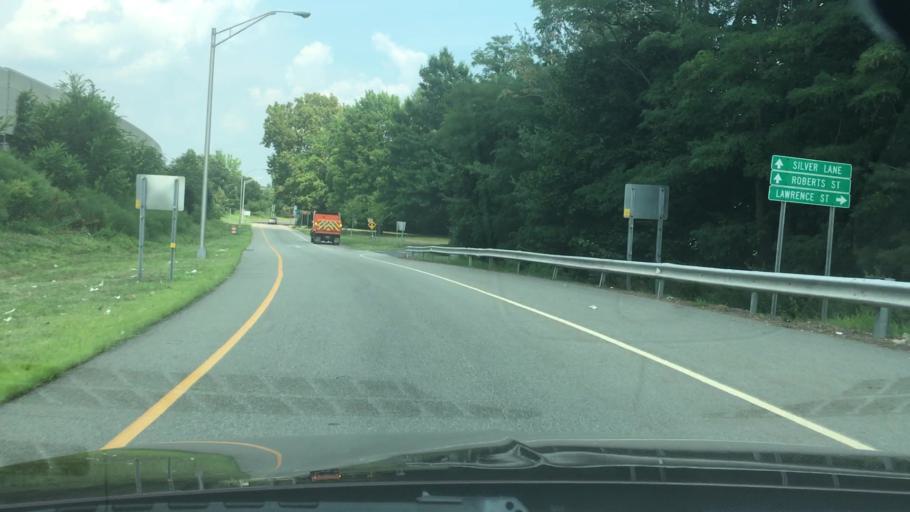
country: US
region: Connecticut
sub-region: Hartford County
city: East Hartford
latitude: 41.7602
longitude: -72.6379
